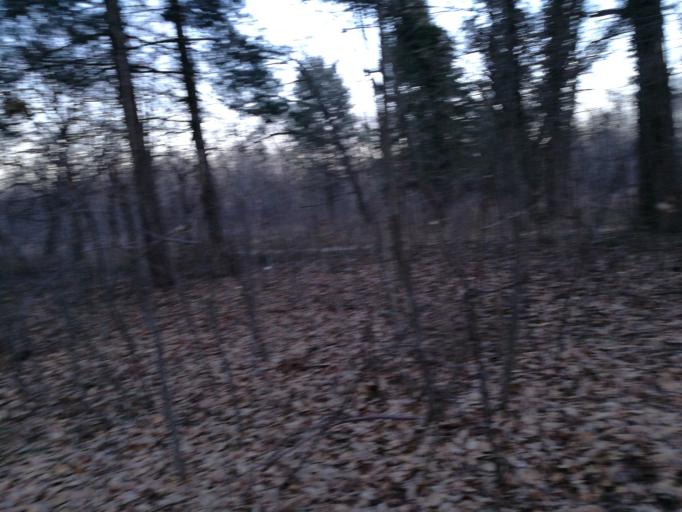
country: RO
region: Ilfov
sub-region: Comuna Otopeni
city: Otopeni
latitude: 44.5139
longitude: 26.0763
